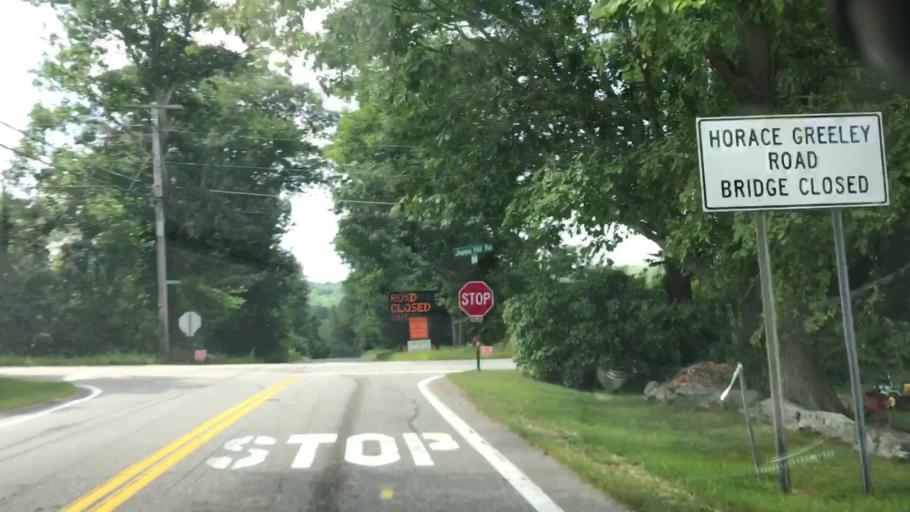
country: US
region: New Hampshire
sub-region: Hillsborough County
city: Bedford
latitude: 42.9244
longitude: -71.5735
